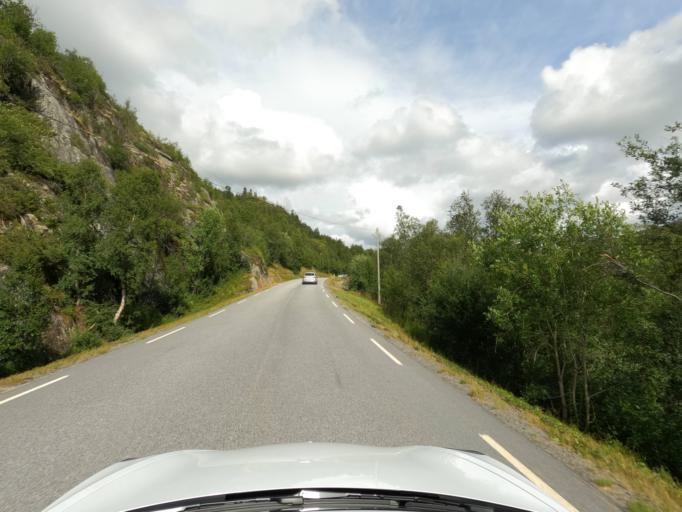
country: NO
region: Telemark
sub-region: Tinn
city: Rjukan
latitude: 59.8356
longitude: 8.3861
